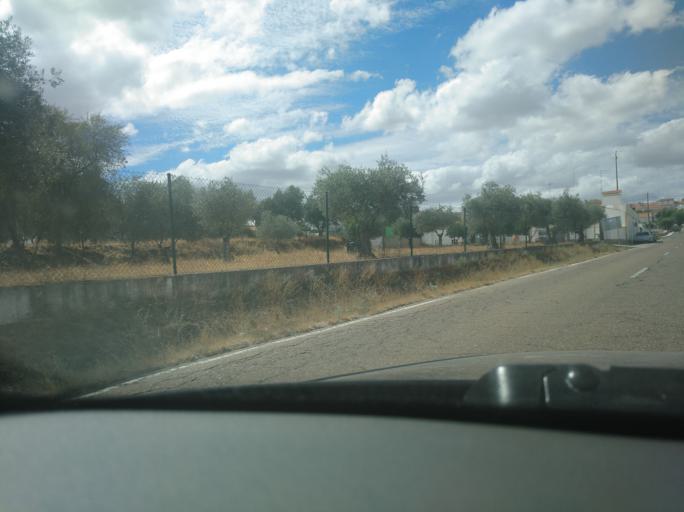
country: PT
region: Portalegre
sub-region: Arronches
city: Arronches
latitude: 39.0498
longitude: -7.4353
